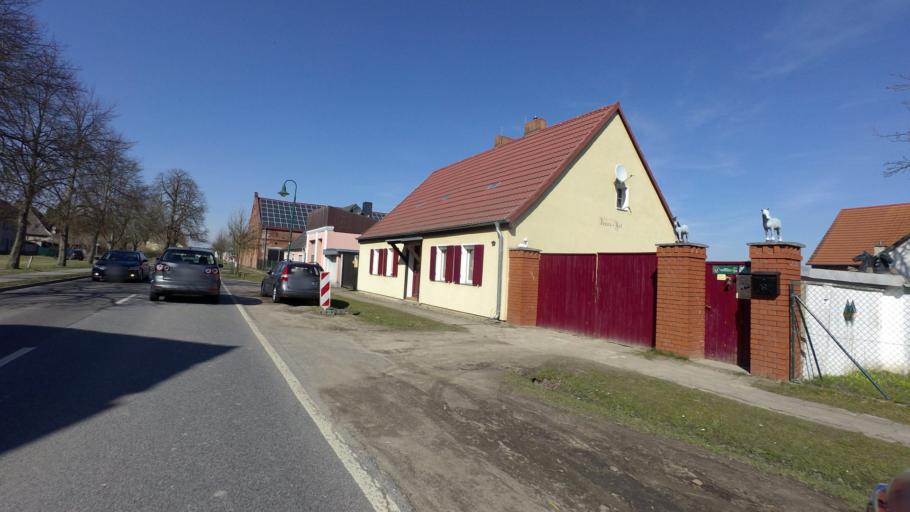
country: DE
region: Brandenburg
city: Eberswalde
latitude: 52.7756
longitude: 13.8369
